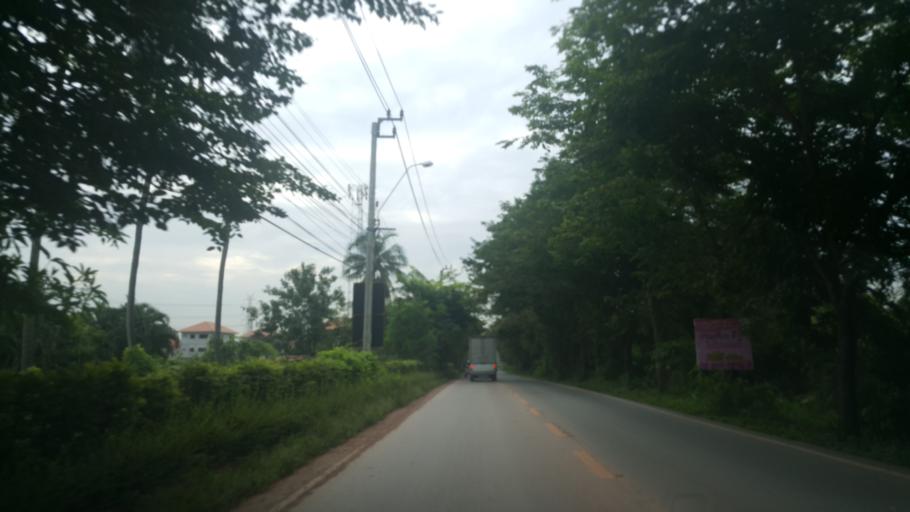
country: TH
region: Bangkok
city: Bang Khae
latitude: 13.6824
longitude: 100.3936
